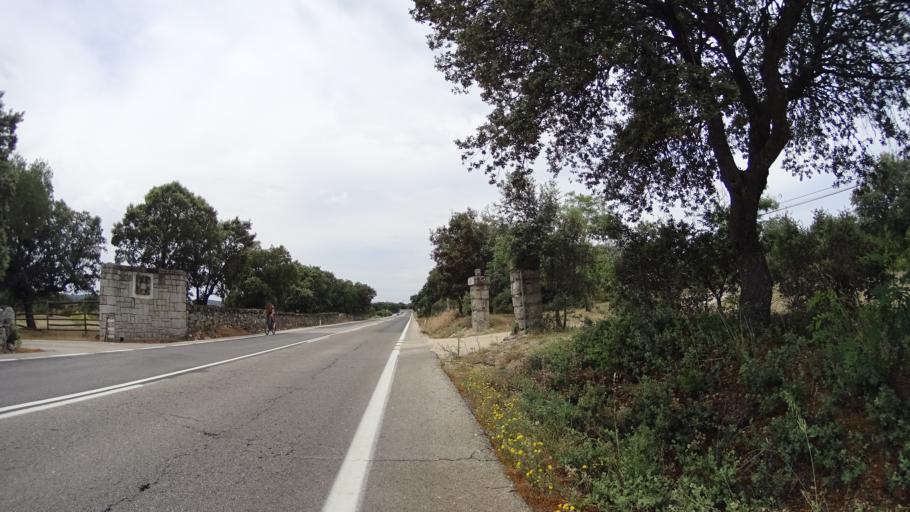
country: ES
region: Madrid
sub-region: Provincia de Madrid
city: Colmenarejo
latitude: 40.5437
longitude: -4.0369
